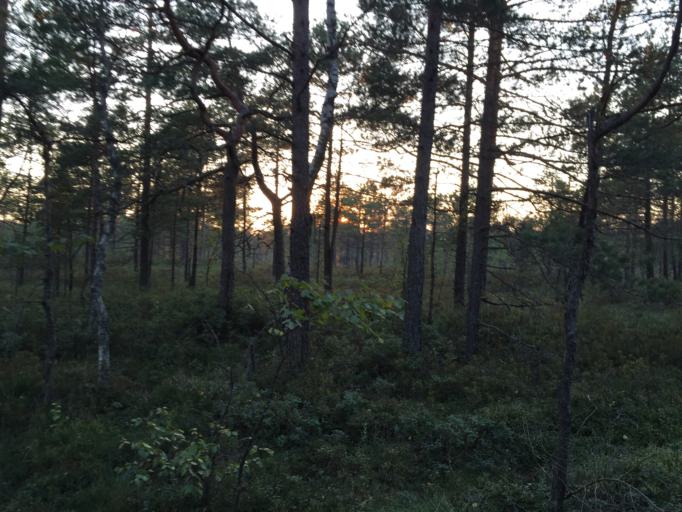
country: LV
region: Limbazu Rajons
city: Limbazi
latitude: 57.5743
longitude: 24.7886
